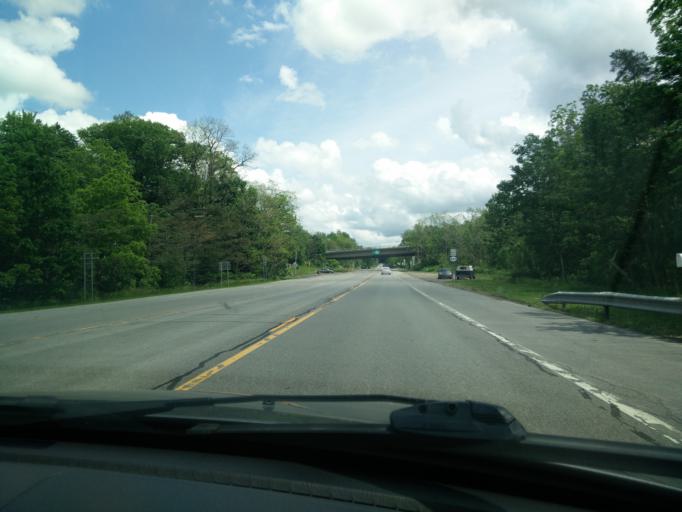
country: US
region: New York
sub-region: Erie County
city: East Aurora
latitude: 42.7675
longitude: -78.5958
